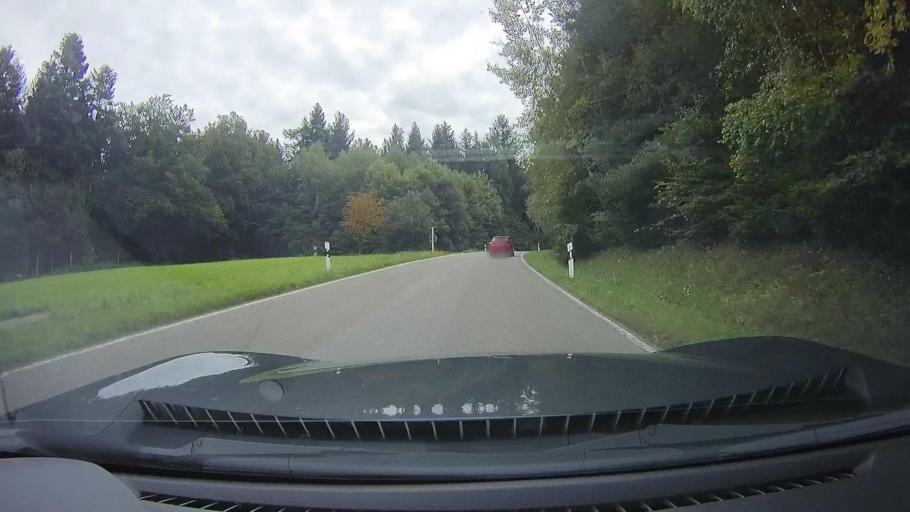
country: DE
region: Baden-Wuerttemberg
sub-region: Regierungsbezirk Stuttgart
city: Althutte
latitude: 48.9211
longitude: 9.5663
